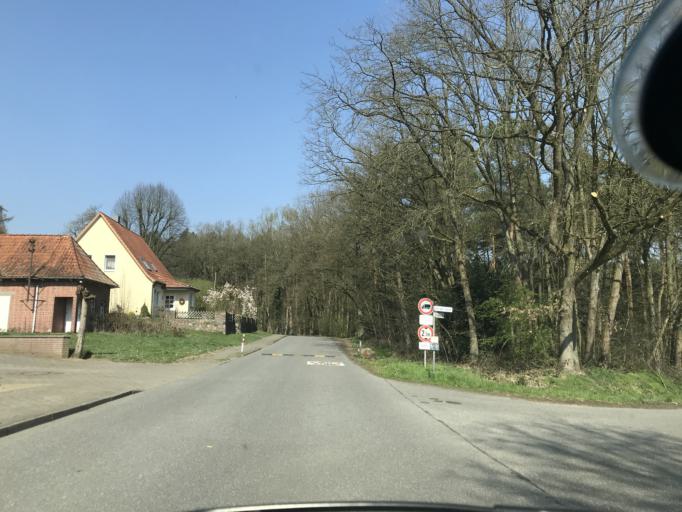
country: DE
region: Lower Saxony
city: Buxtehude
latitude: 53.4500
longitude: 9.7310
